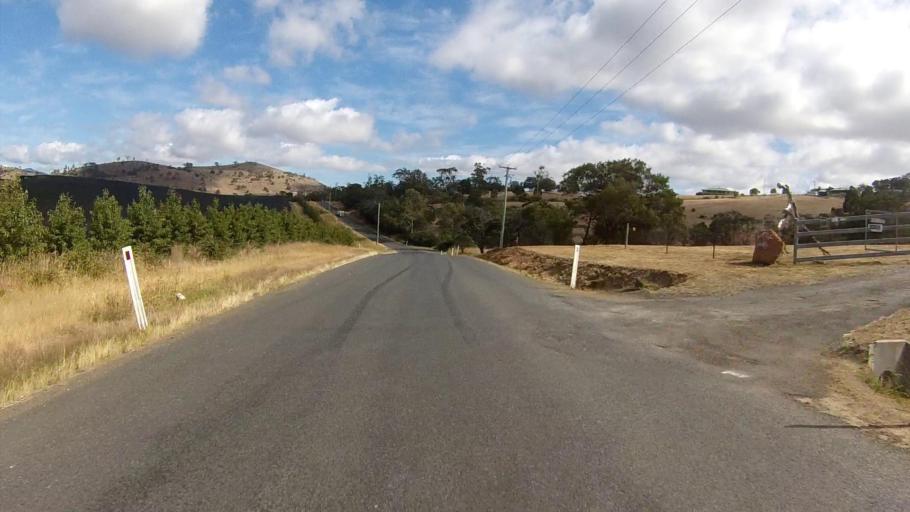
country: AU
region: Tasmania
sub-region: Brighton
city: Old Beach
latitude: -42.7410
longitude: 147.3013
